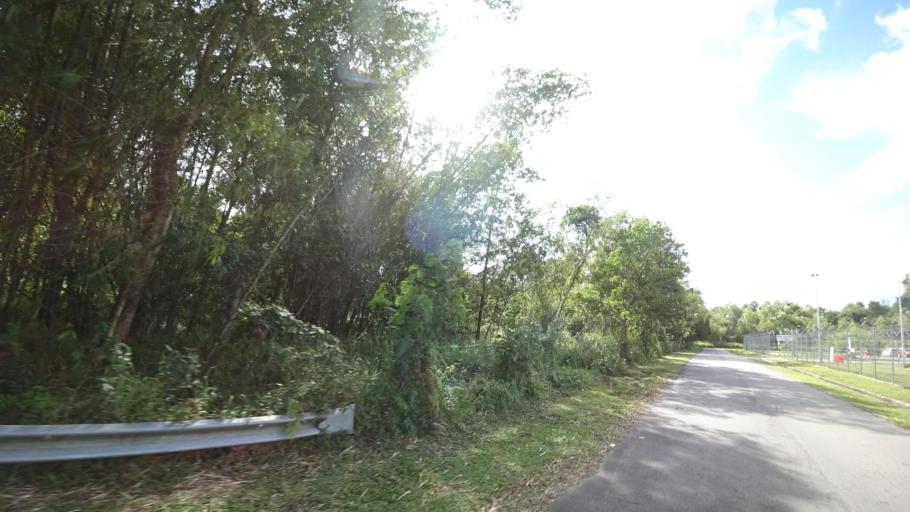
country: BN
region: Brunei and Muara
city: Bandar Seri Begawan
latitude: 4.9006
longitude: 114.9052
